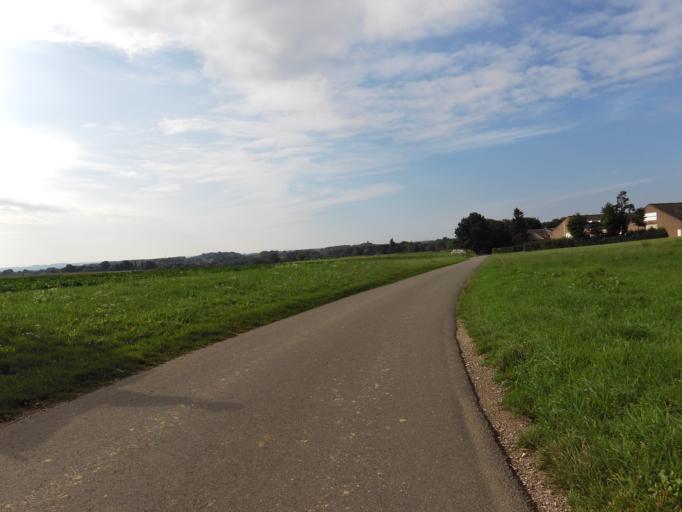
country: NL
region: Limburg
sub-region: Gemeente Nuth
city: Nuth
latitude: 50.9248
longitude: 5.8647
